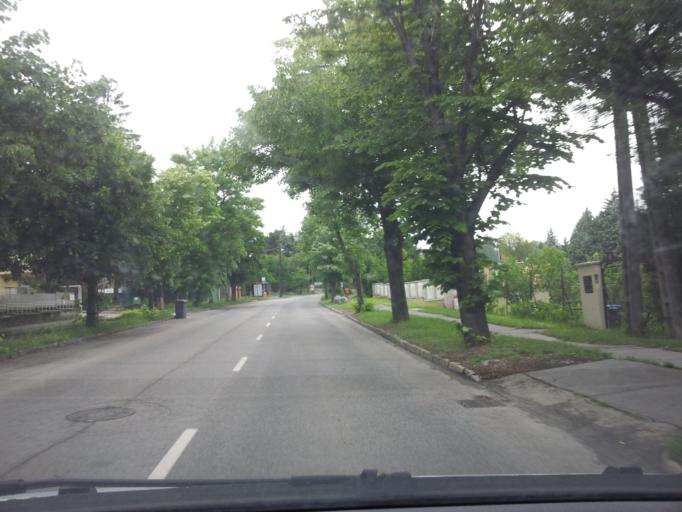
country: HU
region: Budapest
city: Budapest XII. keruelet
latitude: 47.5116
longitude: 18.9983
